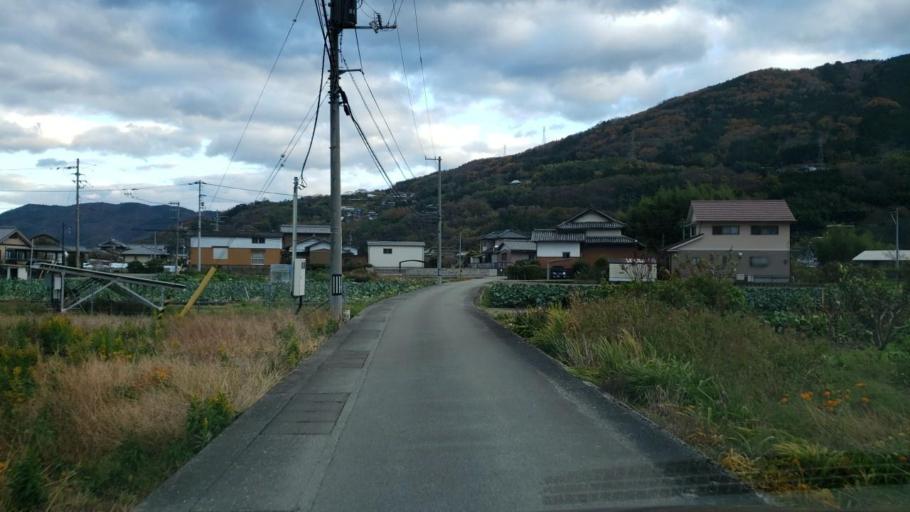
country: JP
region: Tokushima
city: Wakimachi
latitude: 34.0576
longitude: 134.1438
